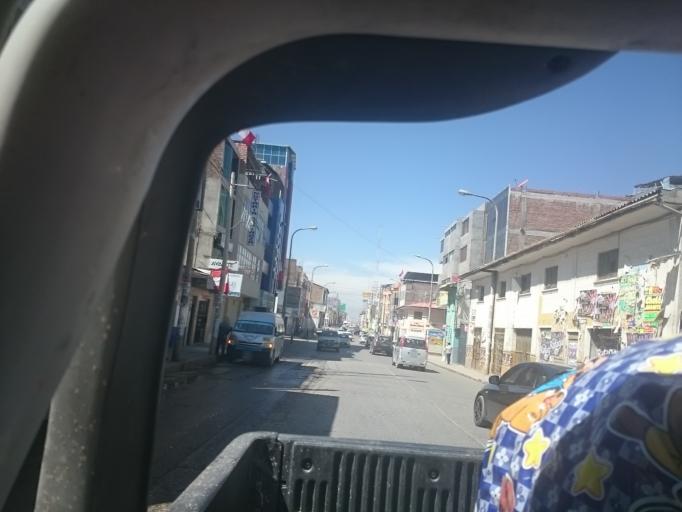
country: PE
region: Junin
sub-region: Provincia de Huancayo
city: El Tambo
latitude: -12.0592
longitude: -75.2161
